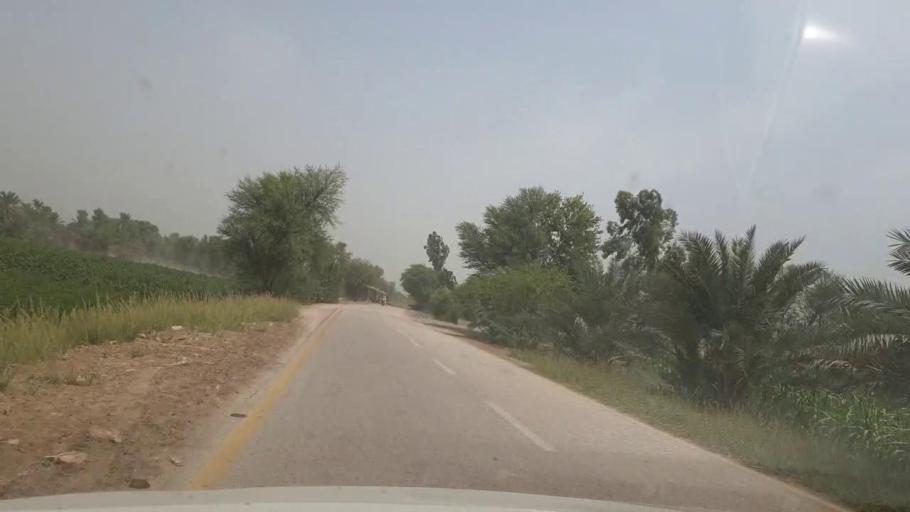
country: PK
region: Sindh
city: Kot Diji
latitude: 27.3795
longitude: 68.6538
